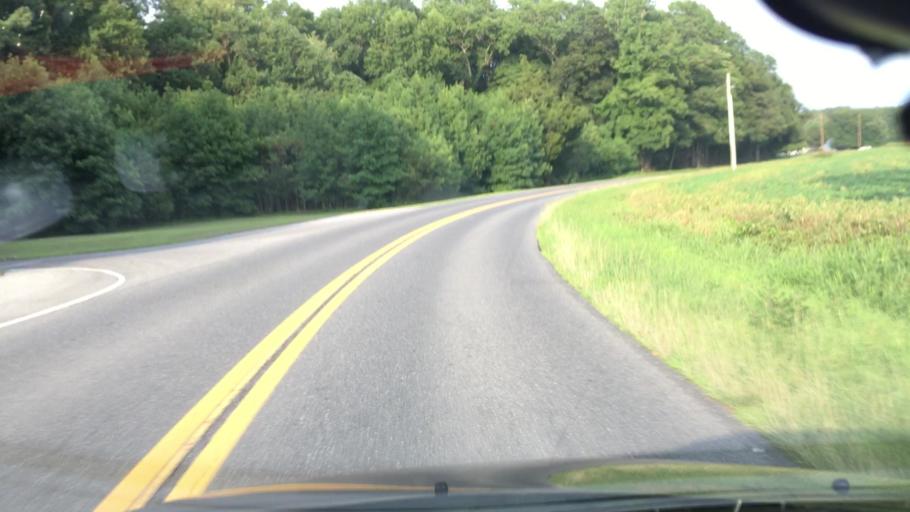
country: US
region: Delaware
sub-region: Sussex County
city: Selbyville
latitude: 38.4687
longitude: -75.1486
